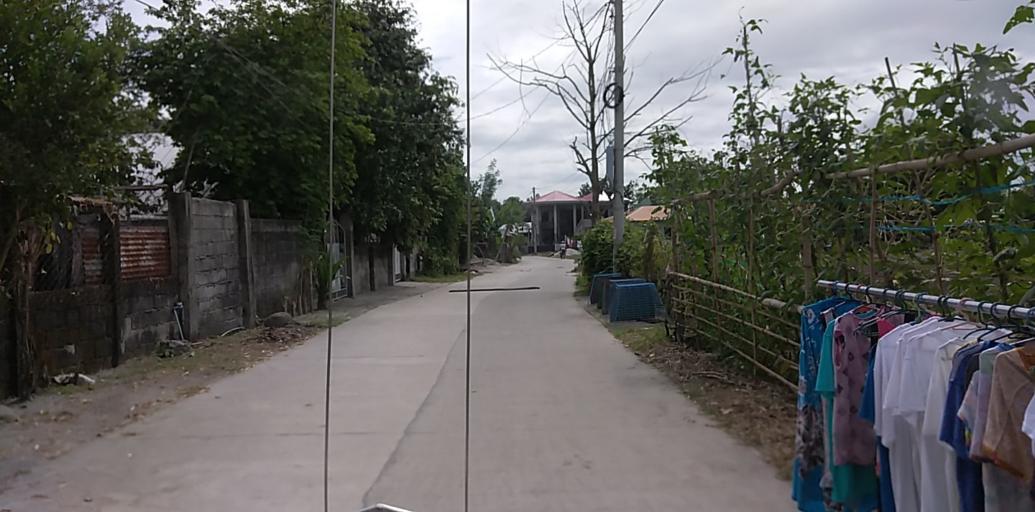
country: PH
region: Central Luzon
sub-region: Province of Pampanga
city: Porac
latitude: 15.0645
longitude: 120.5399
